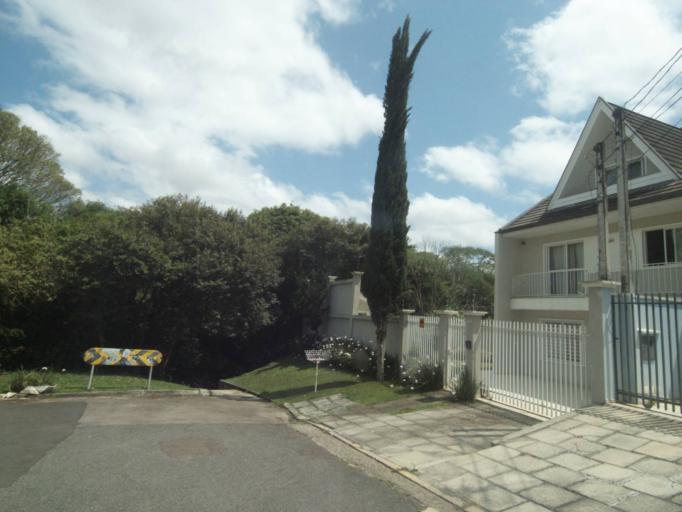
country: BR
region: Parana
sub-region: Curitiba
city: Curitiba
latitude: -25.4159
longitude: -49.2294
